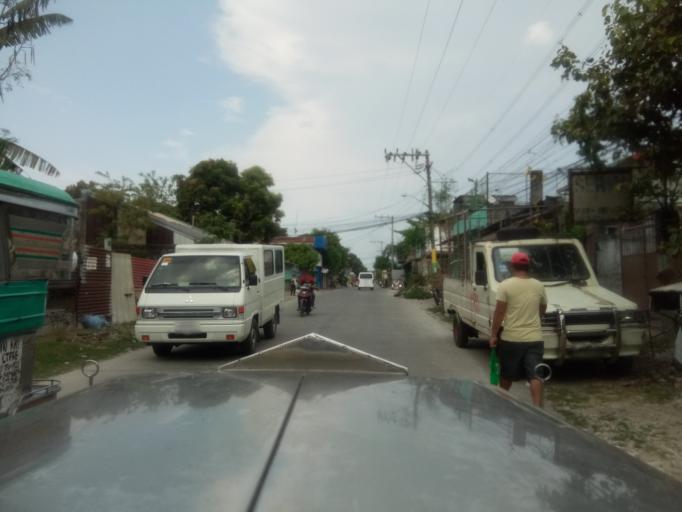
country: PH
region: Calabarzon
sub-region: Province of Cavite
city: Dasmarinas
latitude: 14.3127
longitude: 120.9728
